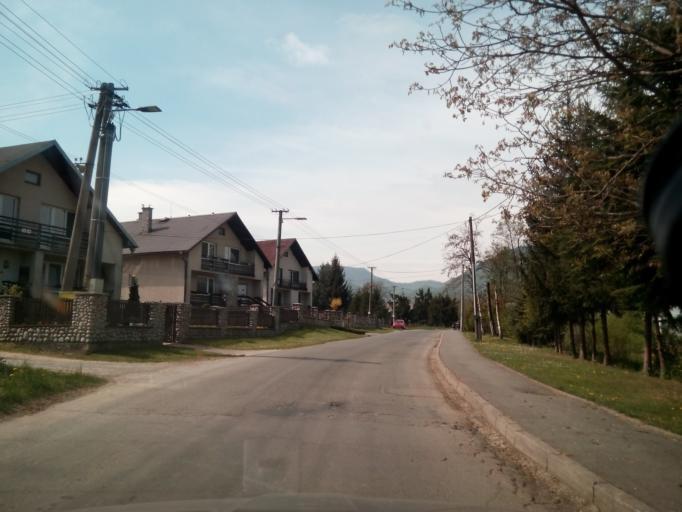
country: SK
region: Presovsky
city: Giraltovce
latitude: 48.9985
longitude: 21.5329
